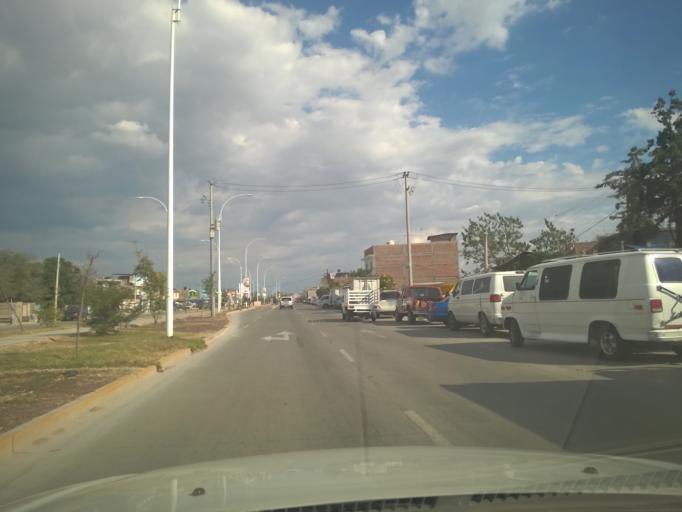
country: MX
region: Guanajuato
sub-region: Leon
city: San Jose de Duran (Los Troncoso)
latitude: 21.0641
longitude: -101.6298
